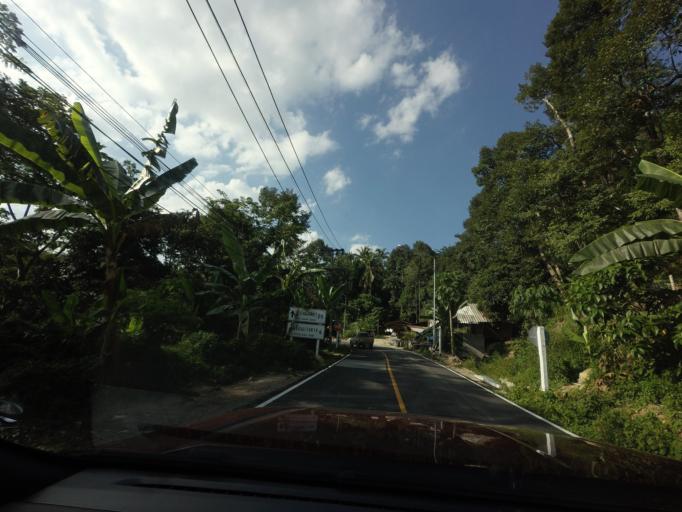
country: TH
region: Yala
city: Than To
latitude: 6.1388
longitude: 101.2977
